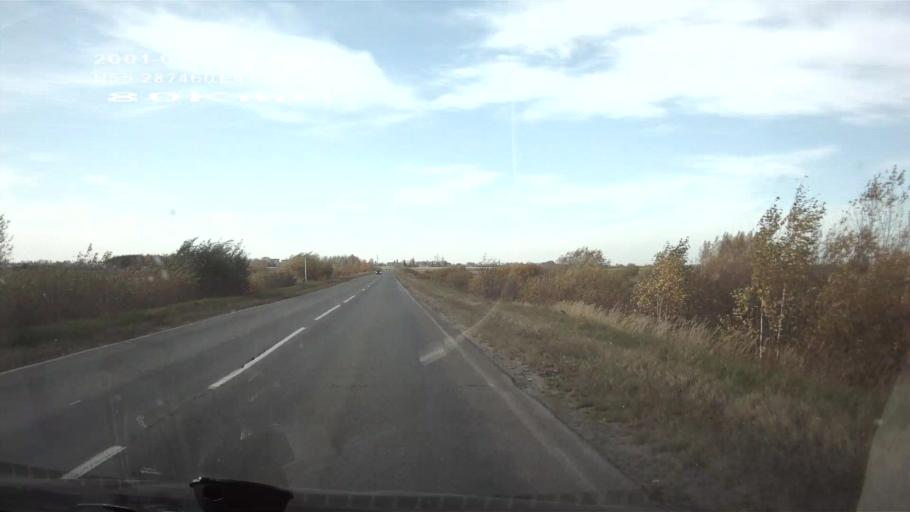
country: RU
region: Chuvashia
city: Ibresi
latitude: 55.2875
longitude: 47.0747
